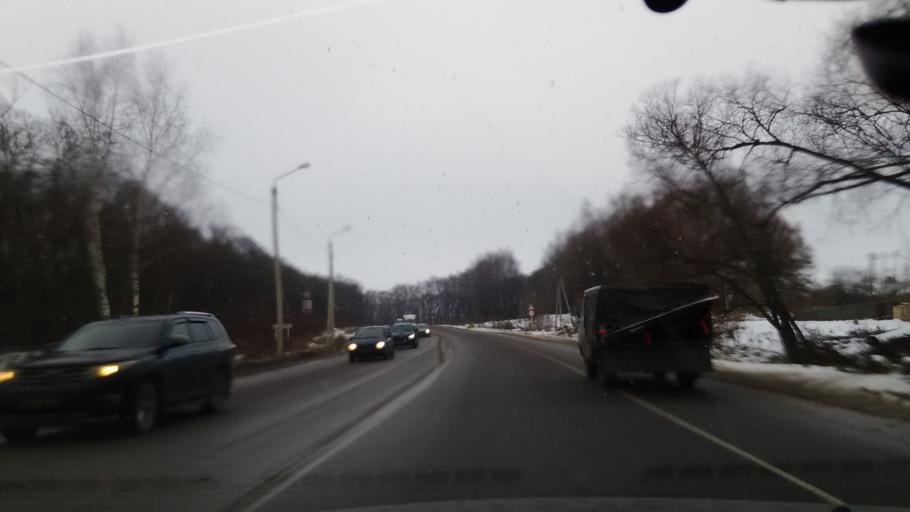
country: RU
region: Tula
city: Skuratovskiy
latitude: 54.1297
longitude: 37.6808
